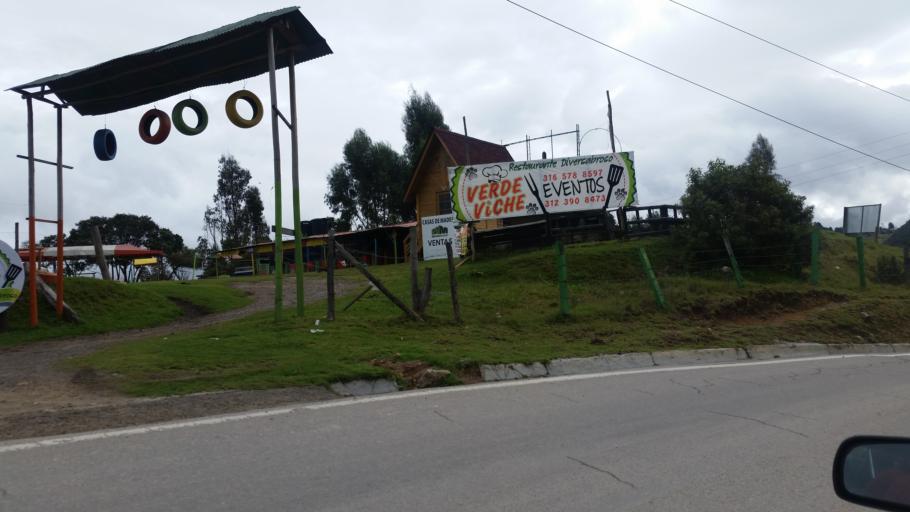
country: CO
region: Cundinamarca
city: La Calera
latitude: 4.7060
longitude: -73.9768
